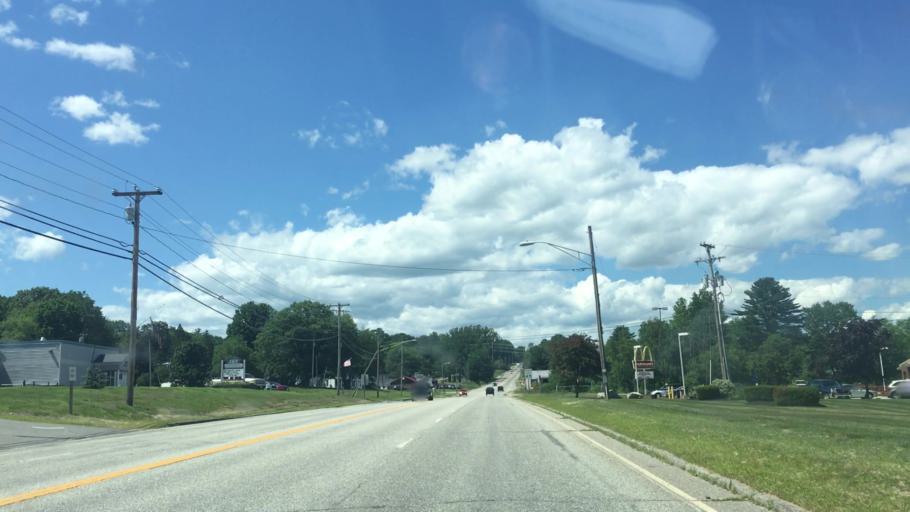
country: US
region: Maine
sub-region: Franklin County
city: Jay
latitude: 44.5055
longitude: -70.2169
